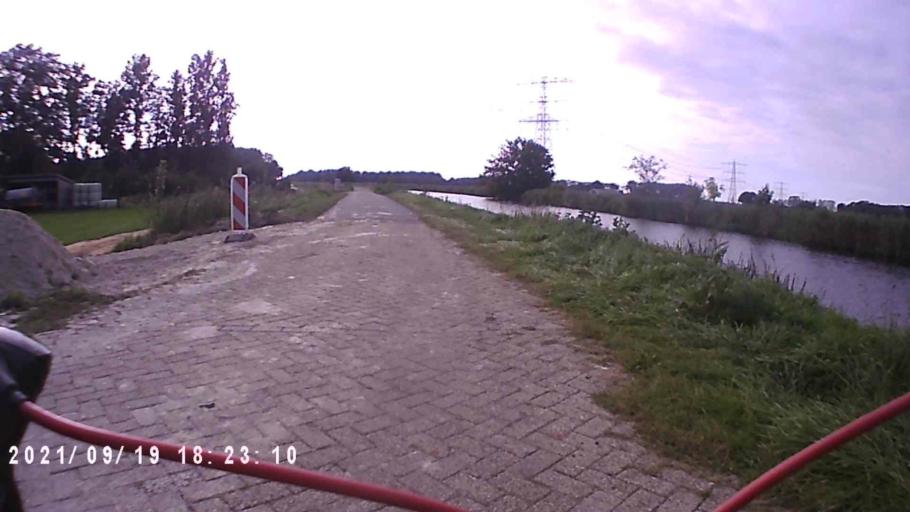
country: NL
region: Groningen
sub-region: Gemeente Appingedam
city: Appingedam
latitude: 53.2754
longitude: 6.8670
